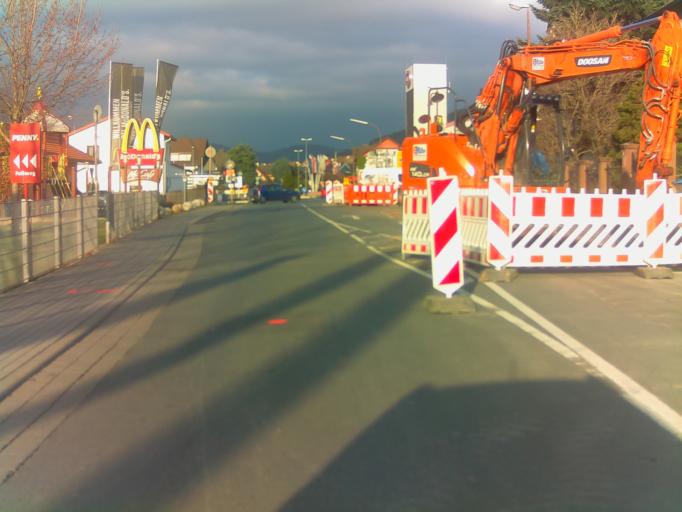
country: DE
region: Bavaria
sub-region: Regierungsbezirk Unterfranken
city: Miltenberg
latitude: 49.7061
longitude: 9.2640
